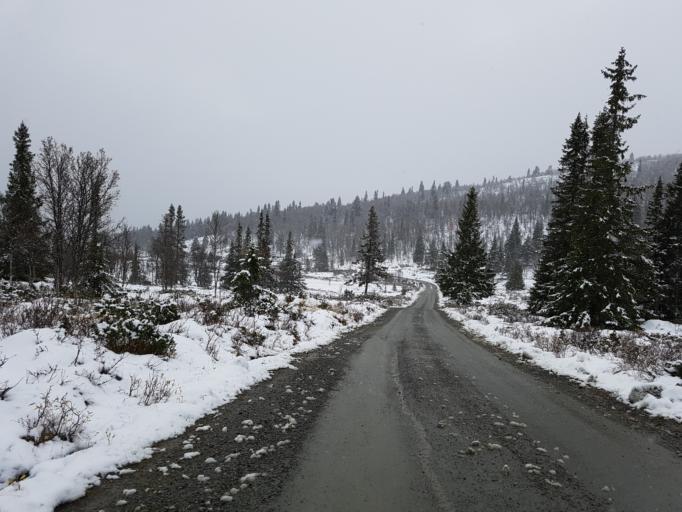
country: NO
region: Oppland
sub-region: Sel
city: Otta
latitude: 61.7966
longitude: 9.7148
